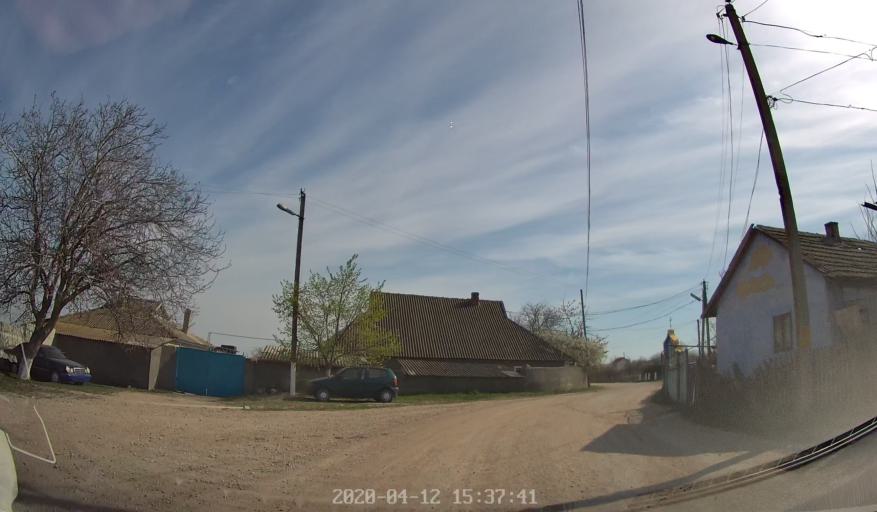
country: MD
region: Telenesti
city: Cocieri
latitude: 47.3214
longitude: 29.0685
